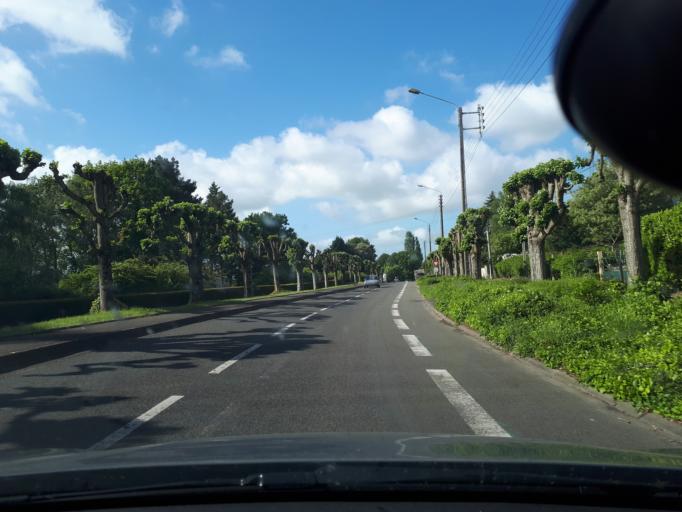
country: FR
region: Pays de la Loire
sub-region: Departement de la Sarthe
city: Change
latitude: 48.0093
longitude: 0.2634
